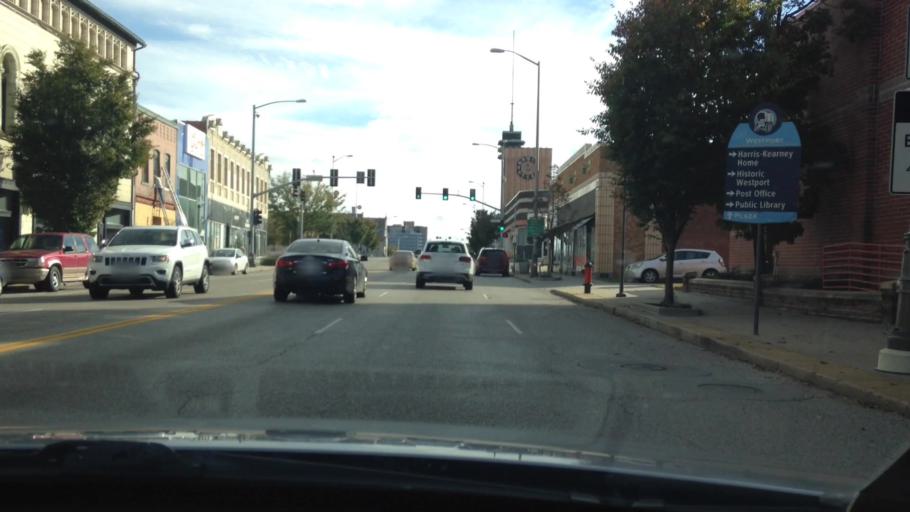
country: US
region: Kansas
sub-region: Johnson County
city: Westwood
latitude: 39.0561
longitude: -94.5862
